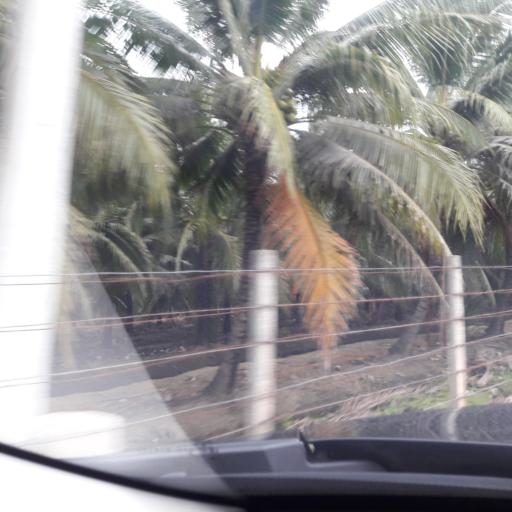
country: TH
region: Ratchaburi
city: Damnoen Saduak
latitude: 13.5672
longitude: 99.9468
